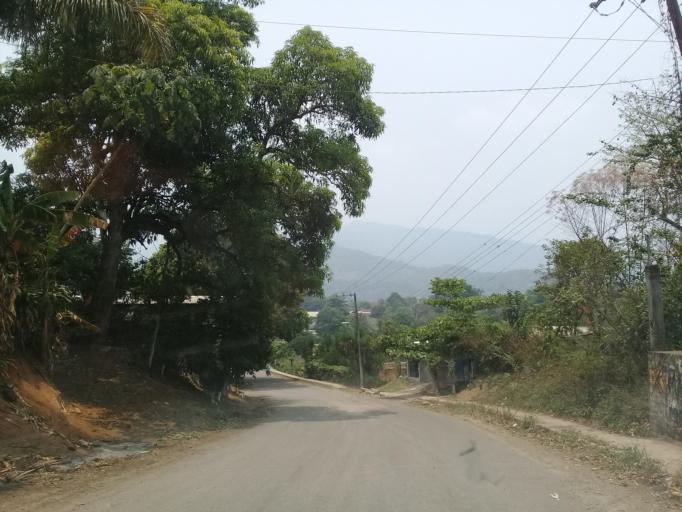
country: MX
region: Veracruz
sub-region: Tezonapa
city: Laguna Chica (Pueblo Nuevo)
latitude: 18.5389
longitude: -96.7324
